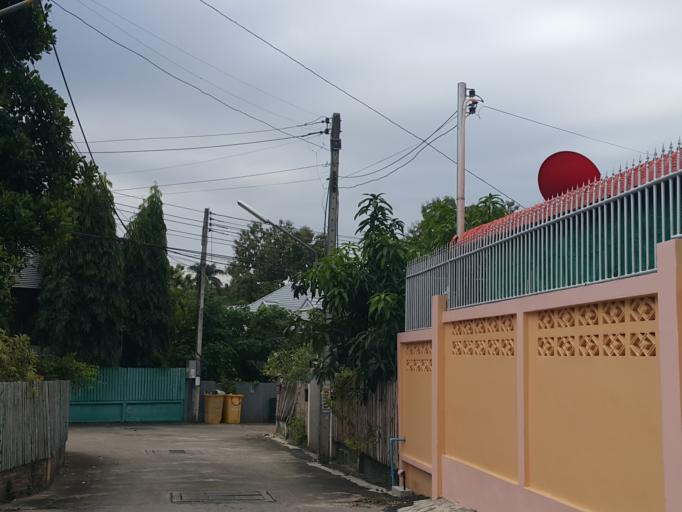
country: TH
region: Lampang
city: Lampang
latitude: 18.2985
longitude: 99.5083
